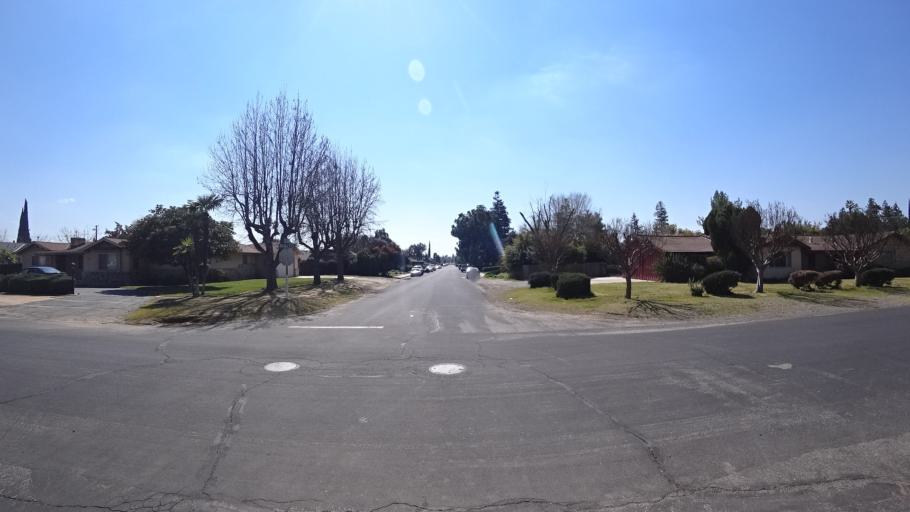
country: US
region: California
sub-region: Fresno County
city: Fresno
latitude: 36.8031
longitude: -119.7928
